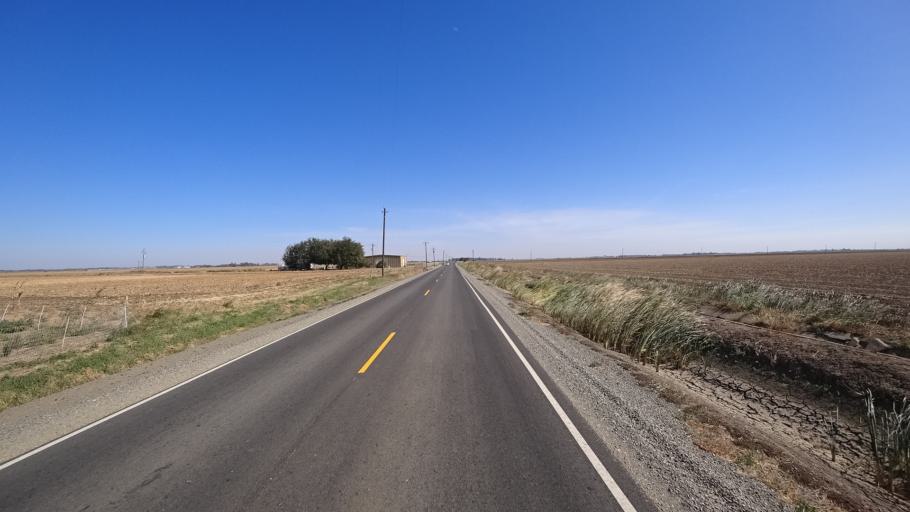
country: US
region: California
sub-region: Yolo County
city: Cottonwood
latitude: 38.6201
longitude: -121.9171
